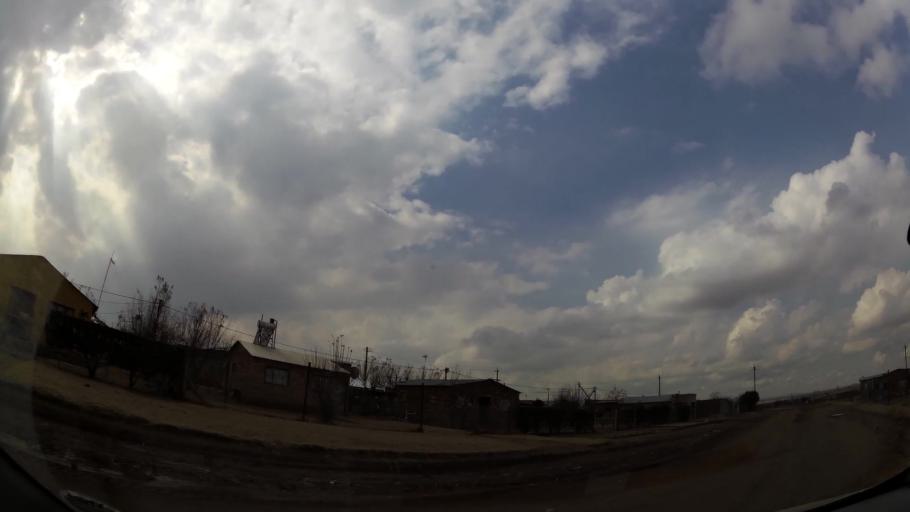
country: ZA
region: Orange Free State
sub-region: Fezile Dabi District Municipality
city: Sasolburg
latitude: -26.8627
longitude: 27.8997
